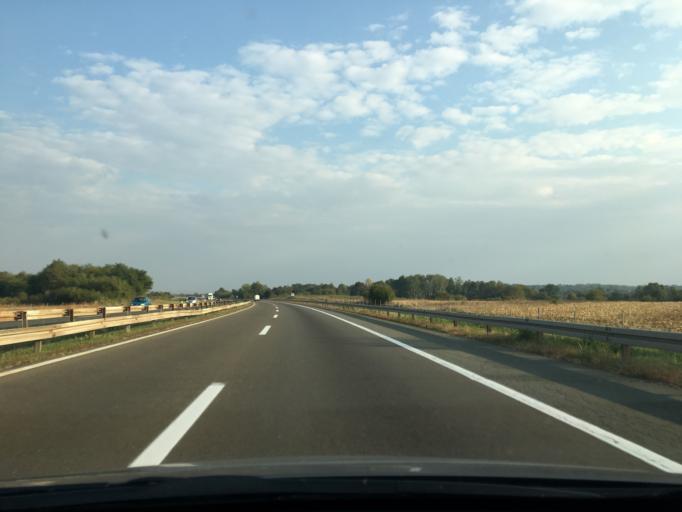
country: RS
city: Lugavcina
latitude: 44.5423
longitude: 20.9904
